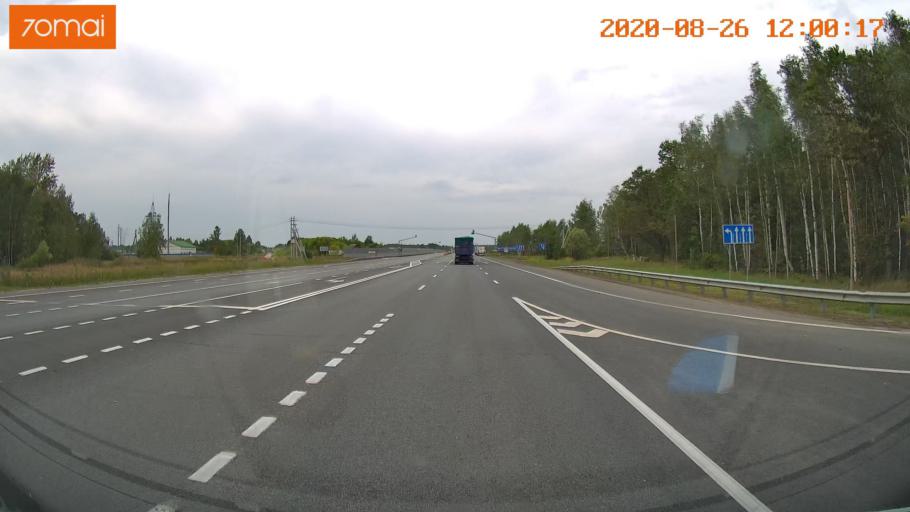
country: RU
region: Rjazan
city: Kiritsy
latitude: 54.2870
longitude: 40.2776
